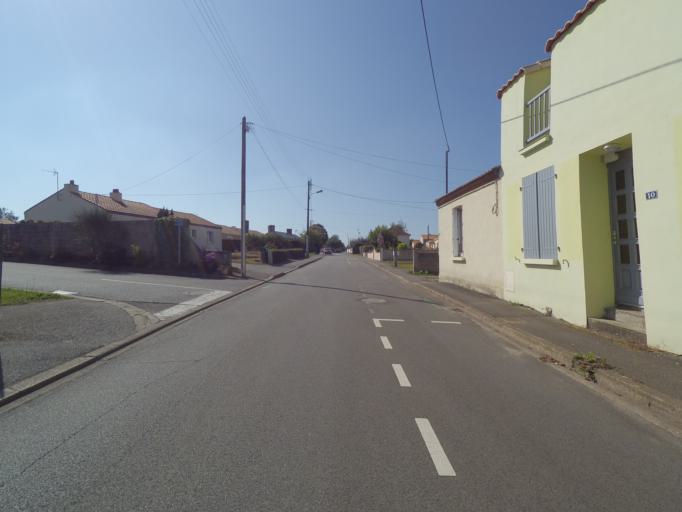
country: FR
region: Pays de la Loire
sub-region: Departement de la Loire-Atlantique
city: Chemere
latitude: 47.1207
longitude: -1.9166
